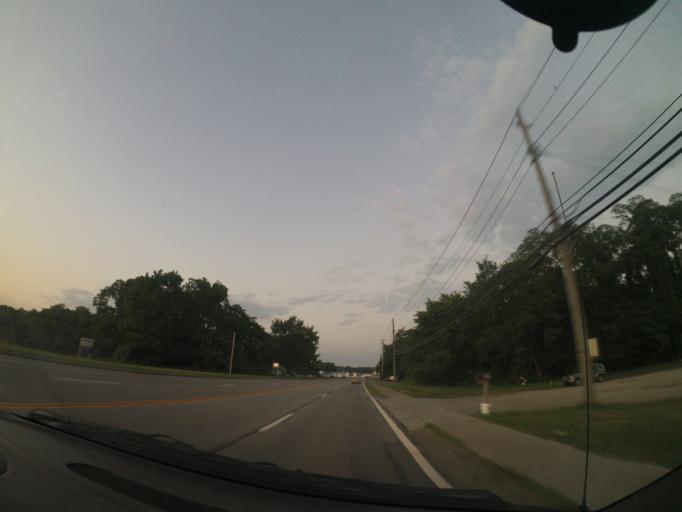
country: US
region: Ohio
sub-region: Lake County
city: North Madison
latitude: 41.8019
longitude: -81.0705
